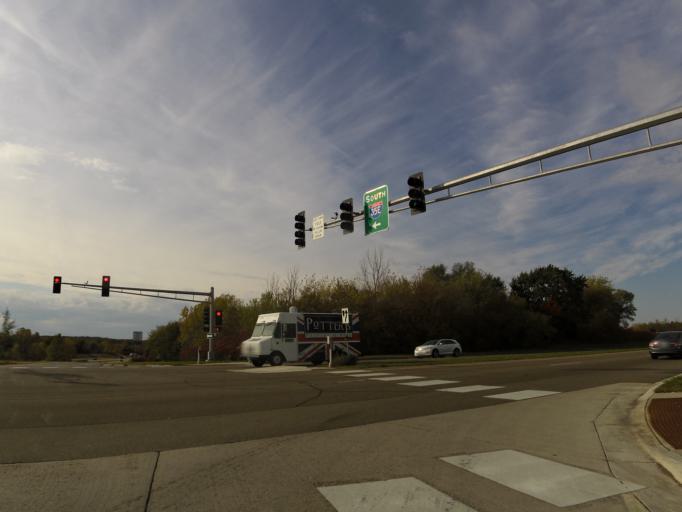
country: US
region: Minnesota
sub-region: Dakota County
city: Eagan
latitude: 44.8047
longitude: -93.1923
